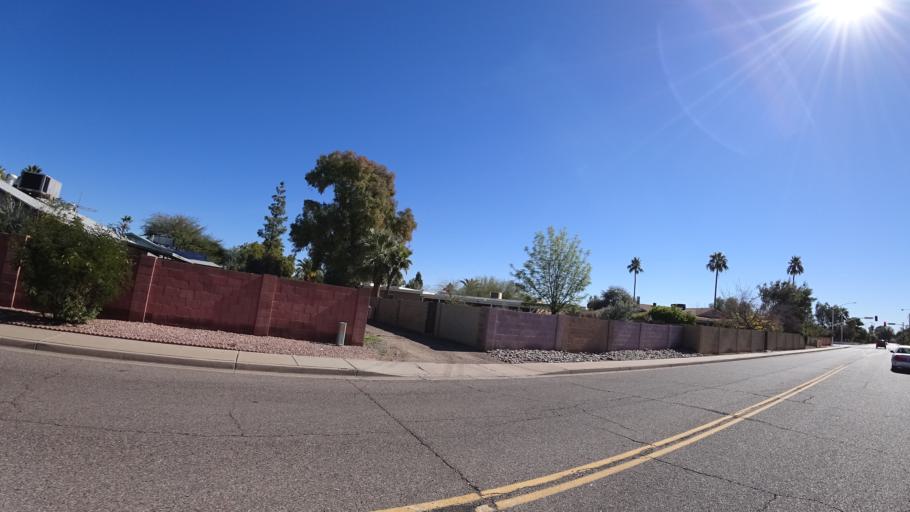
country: US
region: Arizona
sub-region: Maricopa County
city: Scottsdale
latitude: 33.5106
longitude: -111.8960
